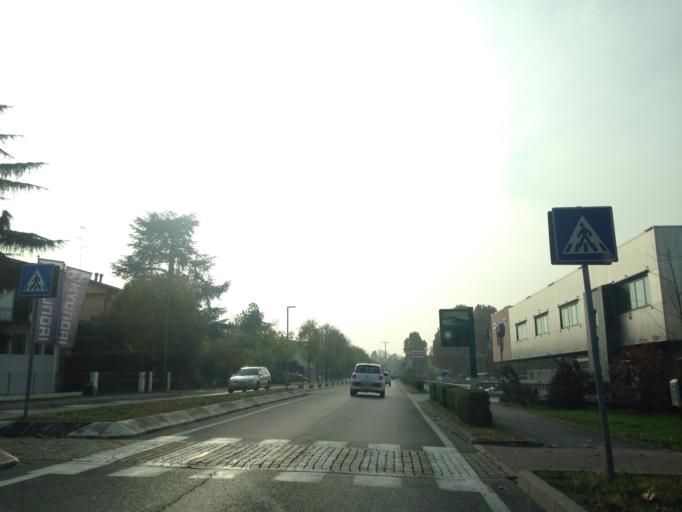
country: IT
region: Veneto
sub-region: Provincia di Treviso
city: Oderzo
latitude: 45.7798
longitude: 12.4969
